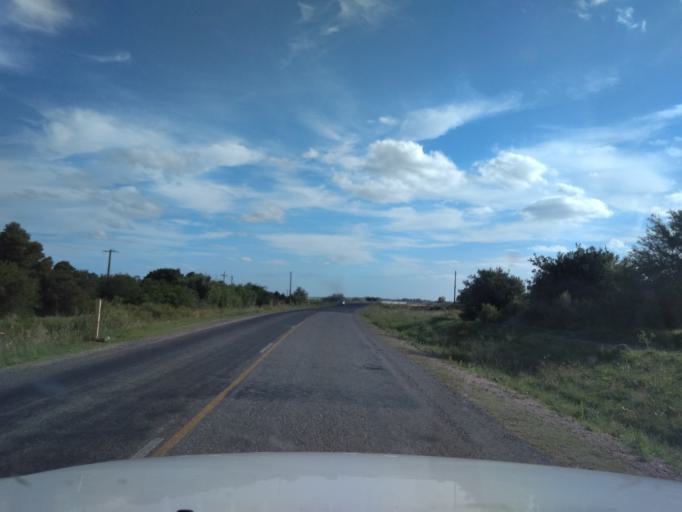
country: UY
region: Canelones
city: San Ramon
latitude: -34.2632
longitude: -55.9277
